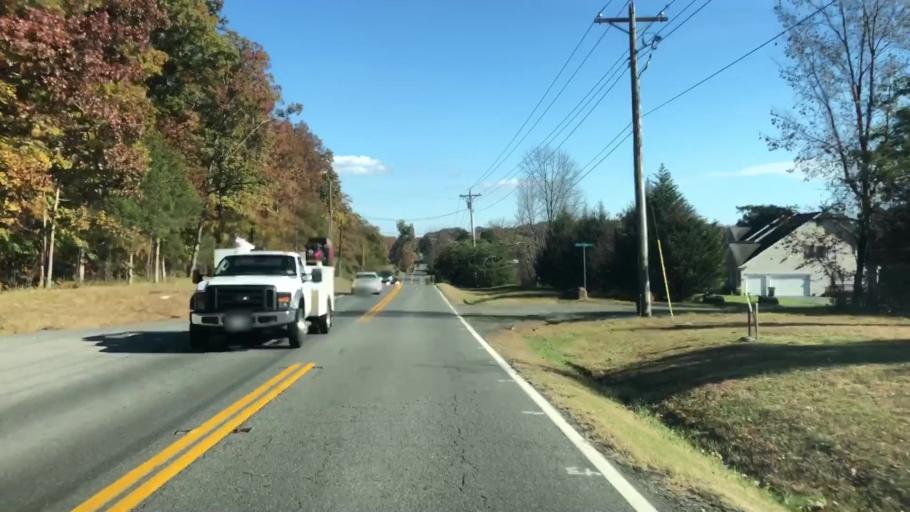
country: US
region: Virginia
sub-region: Prince William County
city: Haymarket
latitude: 38.7531
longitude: -77.6642
